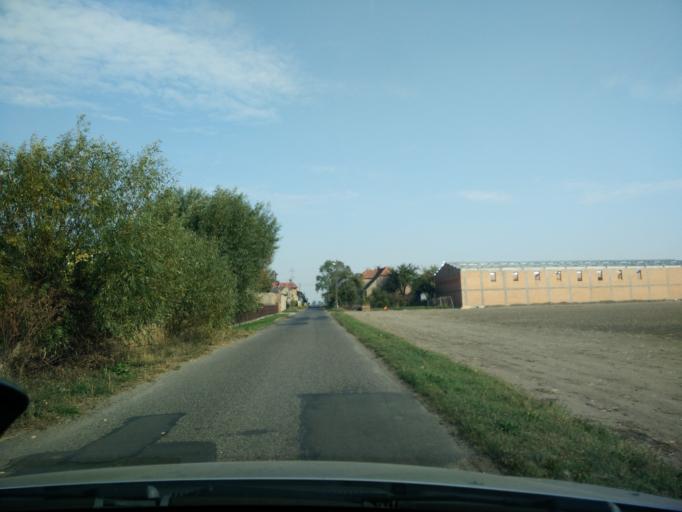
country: PL
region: Greater Poland Voivodeship
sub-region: Powiat sredzki
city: Dominowo
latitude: 52.2928
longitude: 17.3212
